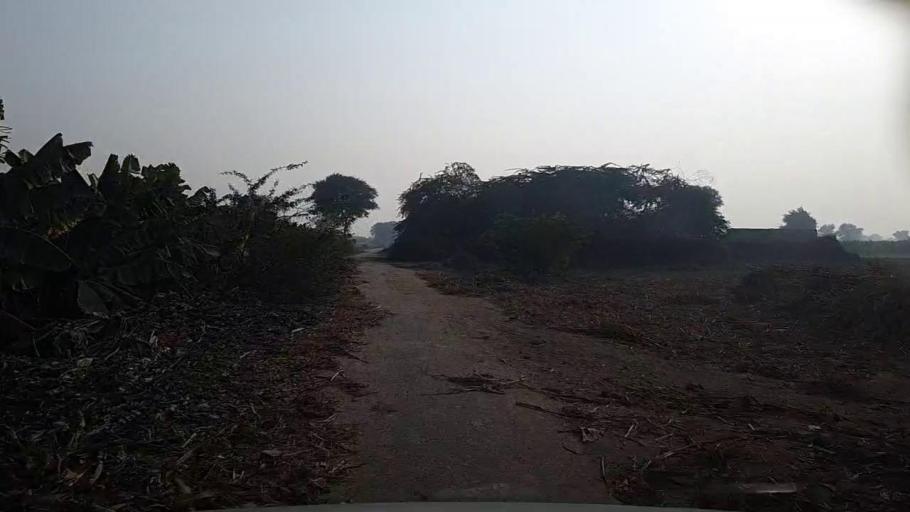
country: PK
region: Sindh
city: Kandiari
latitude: 27.0078
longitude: 68.4949
